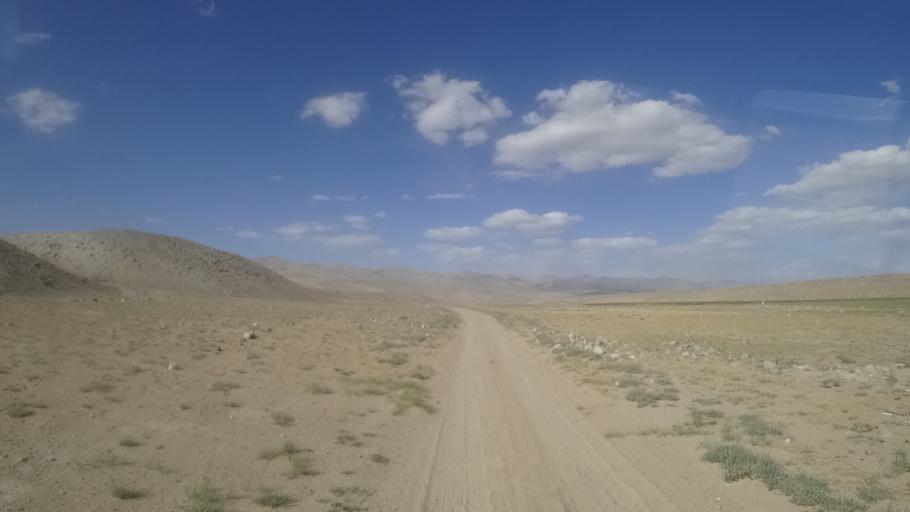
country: AF
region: Badakhshan
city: Khandud
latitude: 37.4188
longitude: 73.2330
